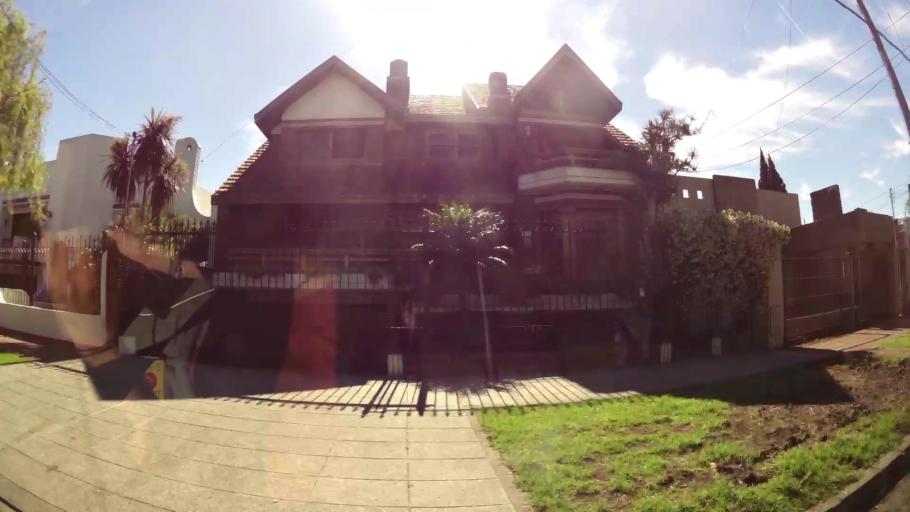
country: AR
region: Buenos Aires
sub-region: Partido de Lomas de Zamora
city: Lomas de Zamora
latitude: -34.7466
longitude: -58.4013
